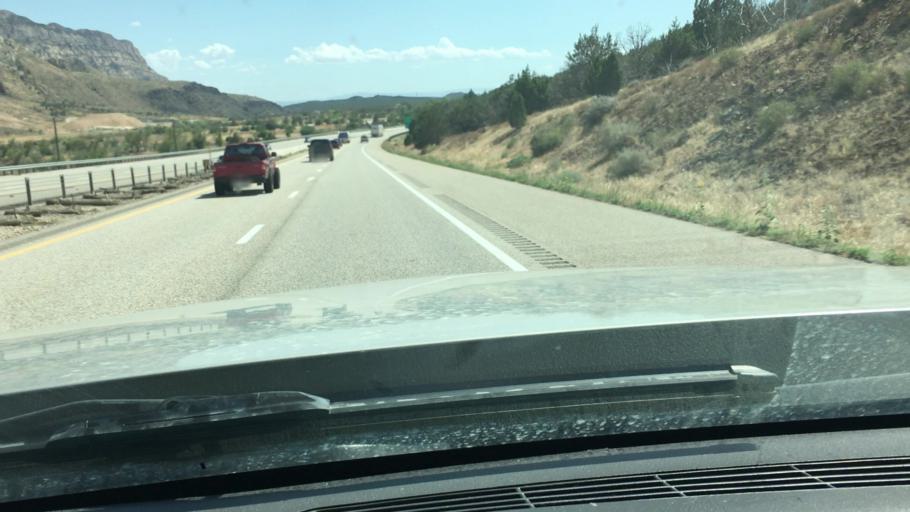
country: US
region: Utah
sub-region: Washington County
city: Toquerville
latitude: 37.3525
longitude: -113.2676
